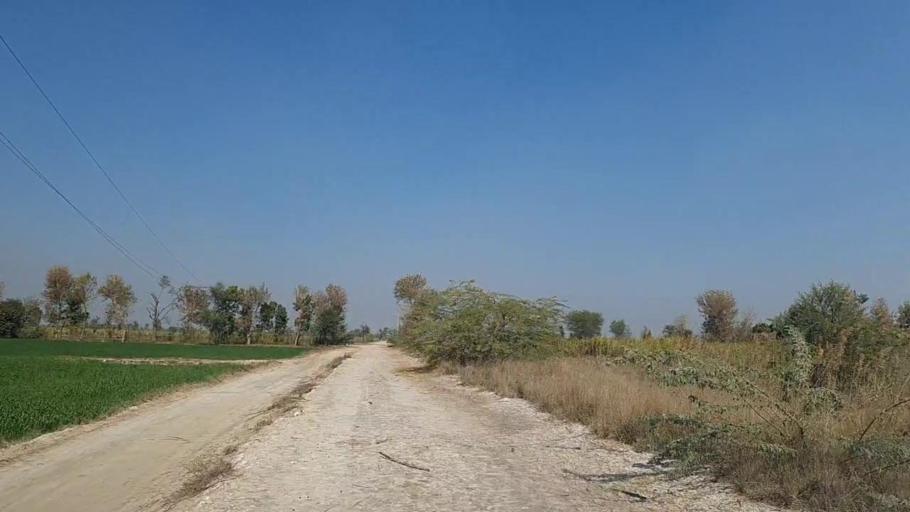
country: PK
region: Sindh
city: Daur
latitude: 26.4879
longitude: 68.3384
